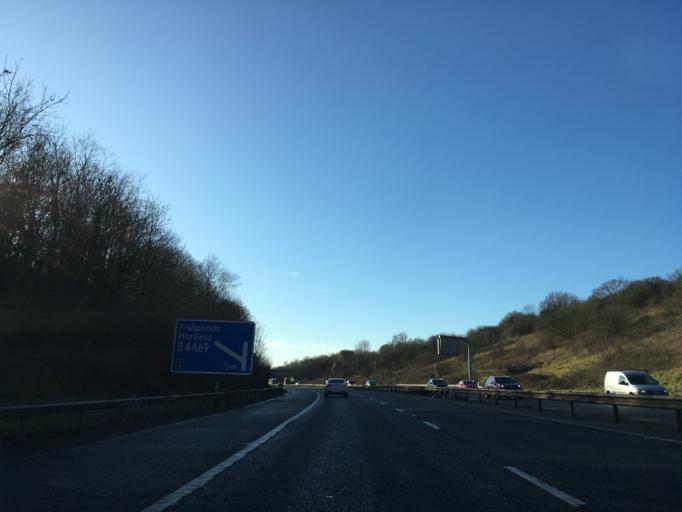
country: GB
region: England
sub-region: South Gloucestershire
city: Stoke Gifford
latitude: 51.4859
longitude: -2.5559
